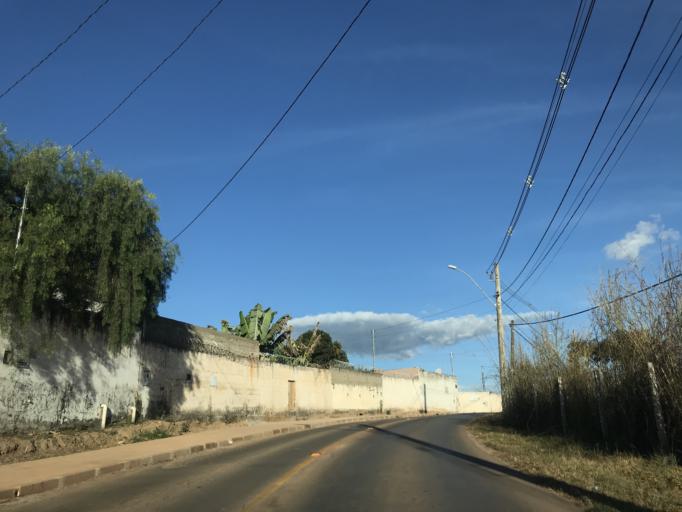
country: BR
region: Federal District
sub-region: Brasilia
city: Brasilia
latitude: -15.8829
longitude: -47.7672
